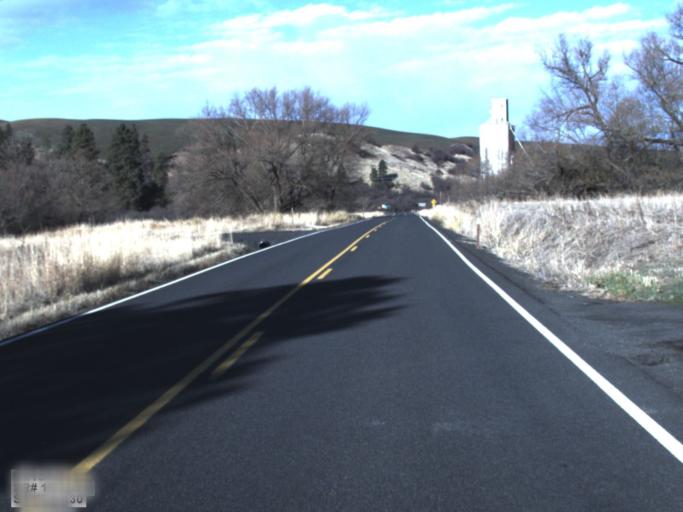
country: US
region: Washington
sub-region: Whitman County
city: Colfax
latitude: 46.7404
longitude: -117.3284
